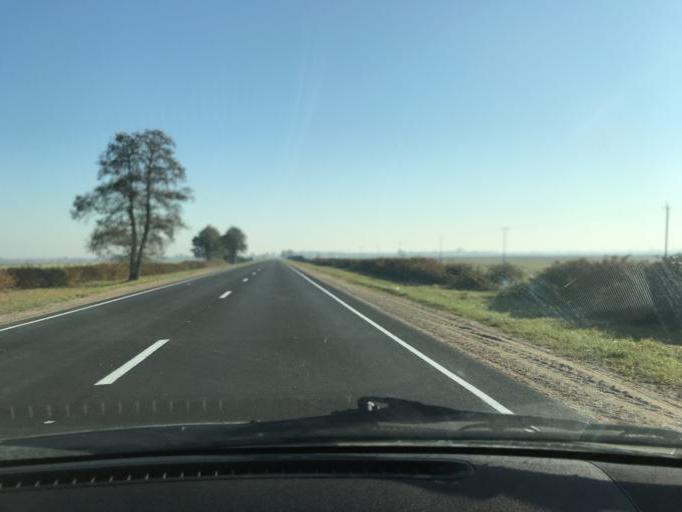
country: BY
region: Brest
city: Baranovichi
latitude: 52.8905
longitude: 25.8209
